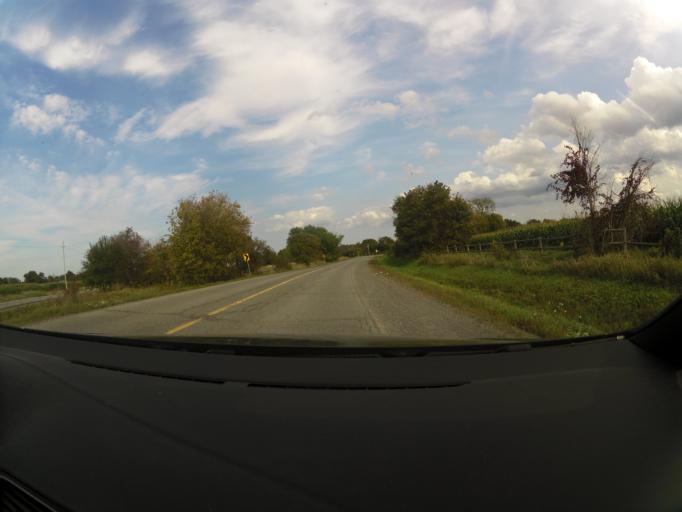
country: CA
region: Ontario
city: Carleton Place
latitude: 45.3556
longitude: -76.1237
